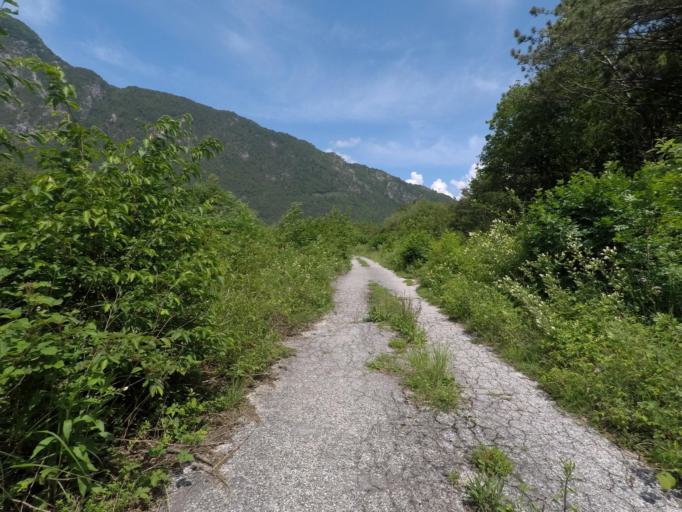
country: IT
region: Friuli Venezia Giulia
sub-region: Provincia di Udine
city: Amaro
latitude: 46.3863
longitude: 13.1408
